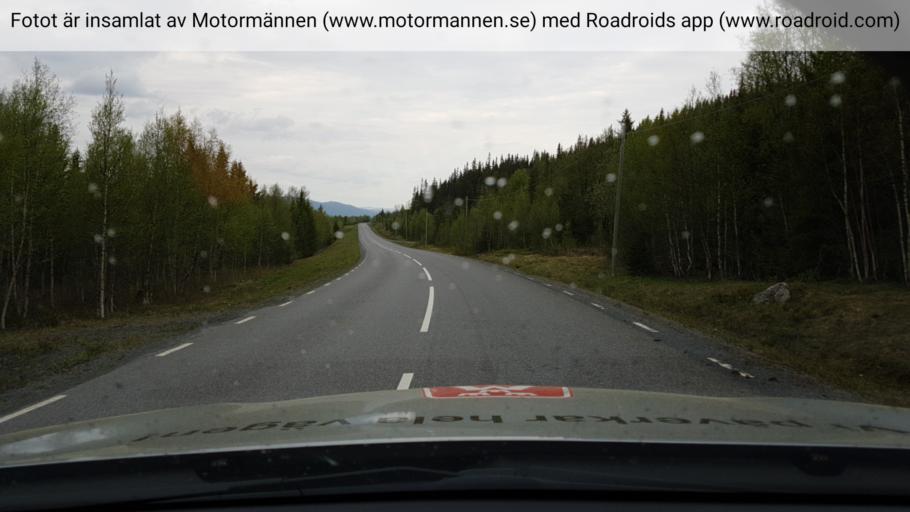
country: SE
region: Jaemtland
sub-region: Are Kommun
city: Are
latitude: 63.5402
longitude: 13.0546
